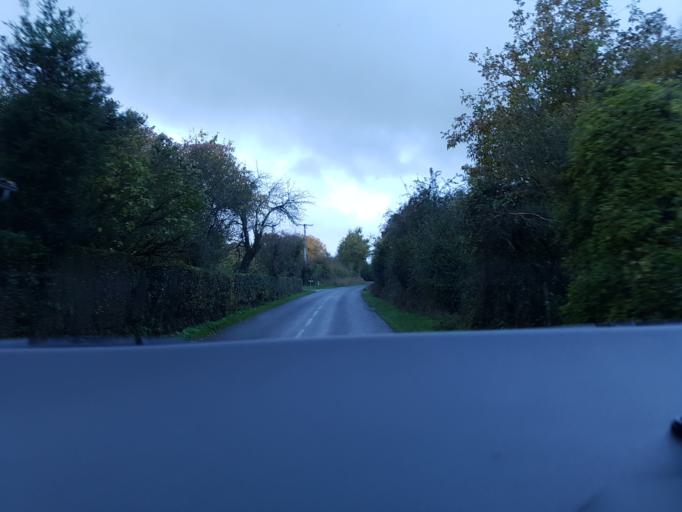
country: FR
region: Poitou-Charentes
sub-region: Departement des Deux-Sevres
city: Lezay
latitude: 46.2495
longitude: -0.0189
